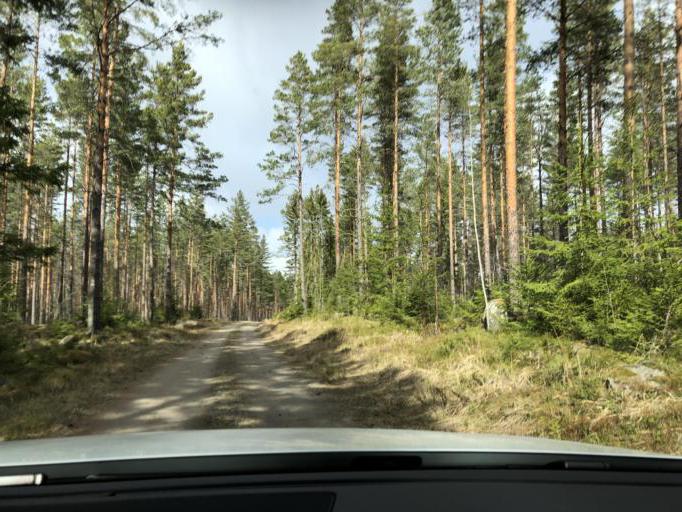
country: SE
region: Gaevleborg
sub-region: Gavle Kommun
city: Hedesunda
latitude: 60.3283
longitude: 17.1065
